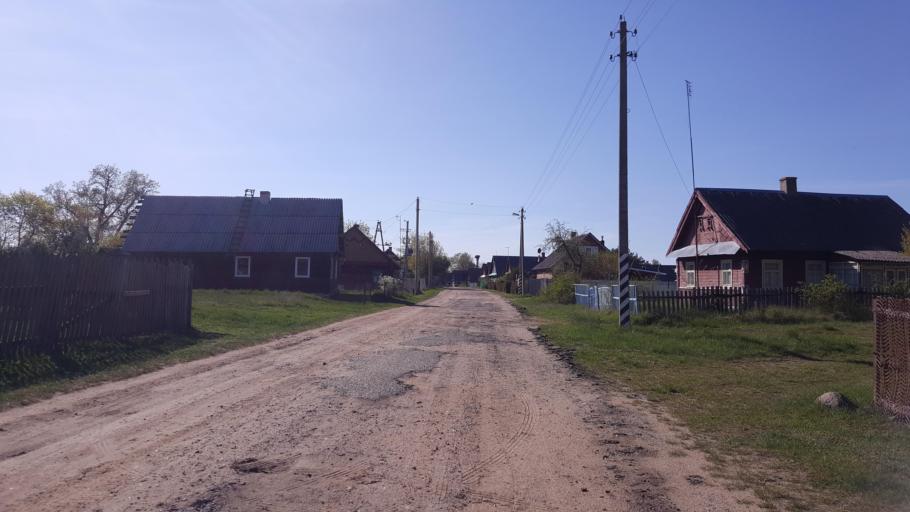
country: BY
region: Brest
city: Kamyanyets
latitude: 52.4400
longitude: 23.8945
